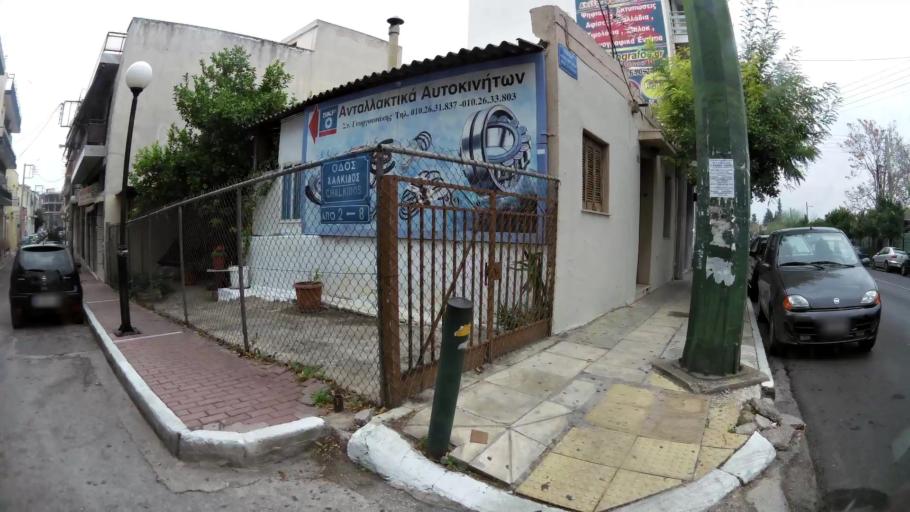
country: GR
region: Attica
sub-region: Nomarchia Athinas
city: Agioi Anargyroi
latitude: 38.0289
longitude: 23.7173
